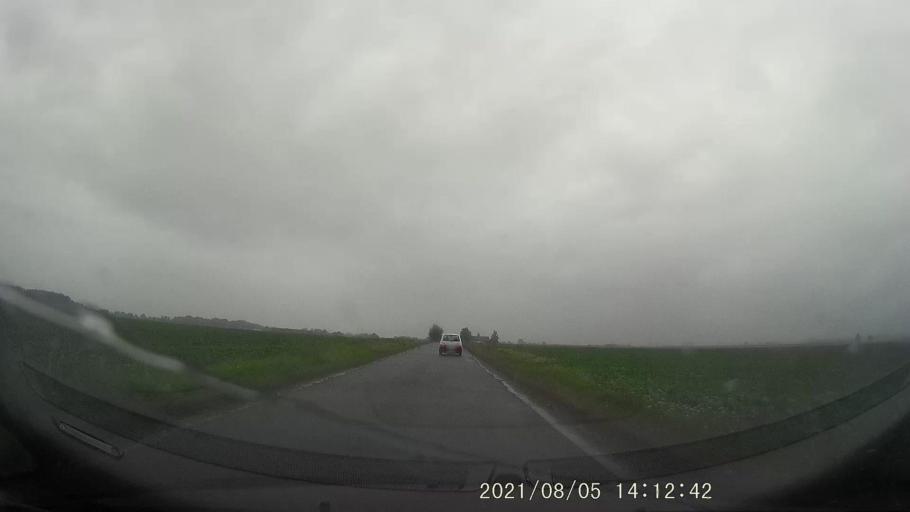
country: PL
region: Opole Voivodeship
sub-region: Powiat krapkowicki
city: Strzeleczki
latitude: 50.4686
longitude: 17.7577
